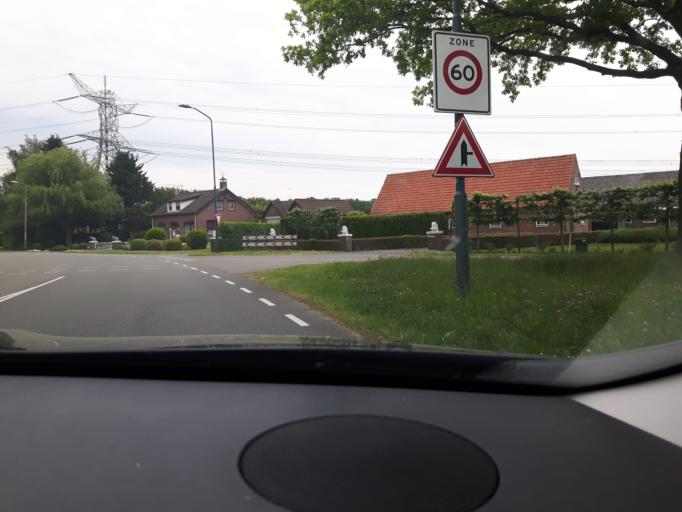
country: NL
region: North Brabant
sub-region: Gemeente Bergen op Zoom
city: Lepelstraat
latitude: 51.5424
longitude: 4.2775
